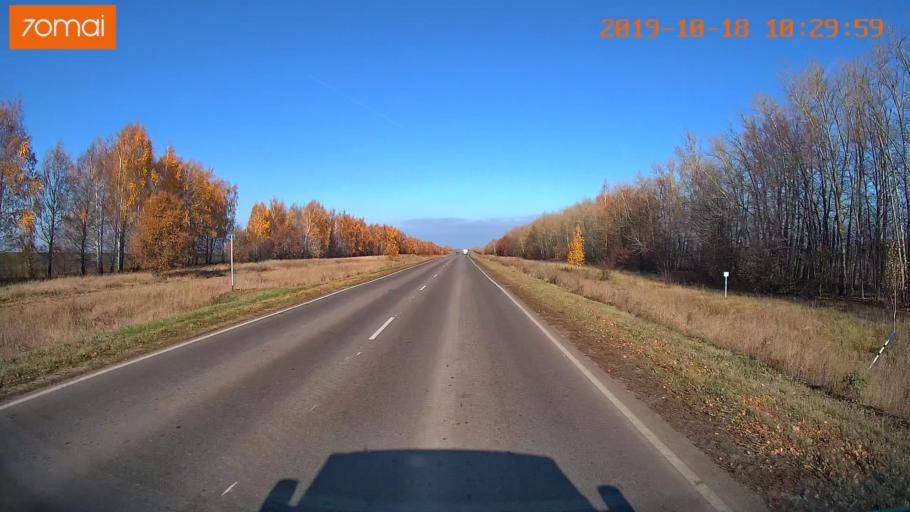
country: RU
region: Tula
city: Kurkino
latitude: 53.4589
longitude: 38.6495
